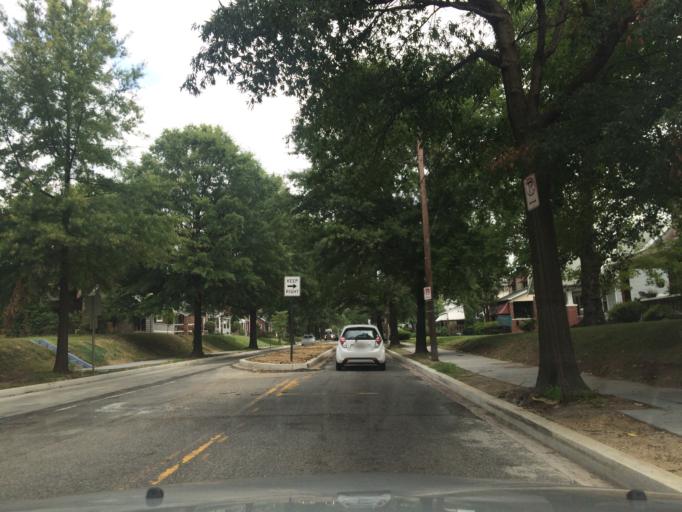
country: US
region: Maryland
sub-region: Prince George's County
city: Silver Hill
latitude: 38.8595
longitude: -76.9588
